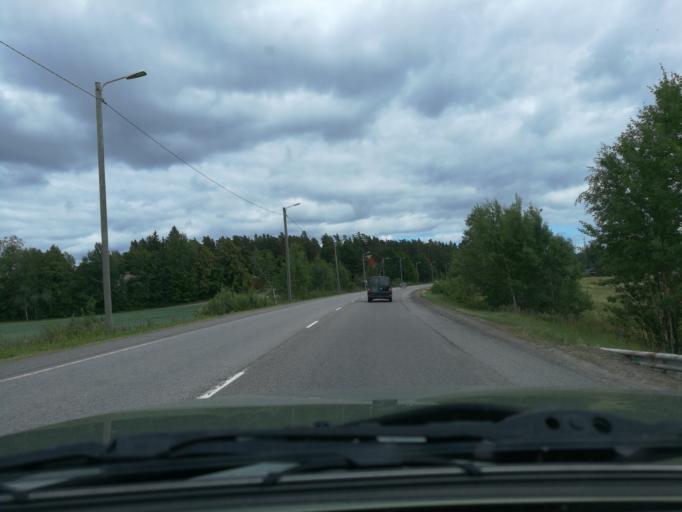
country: FI
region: Uusimaa
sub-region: Helsinki
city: Vantaa
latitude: 60.3136
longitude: 25.0875
